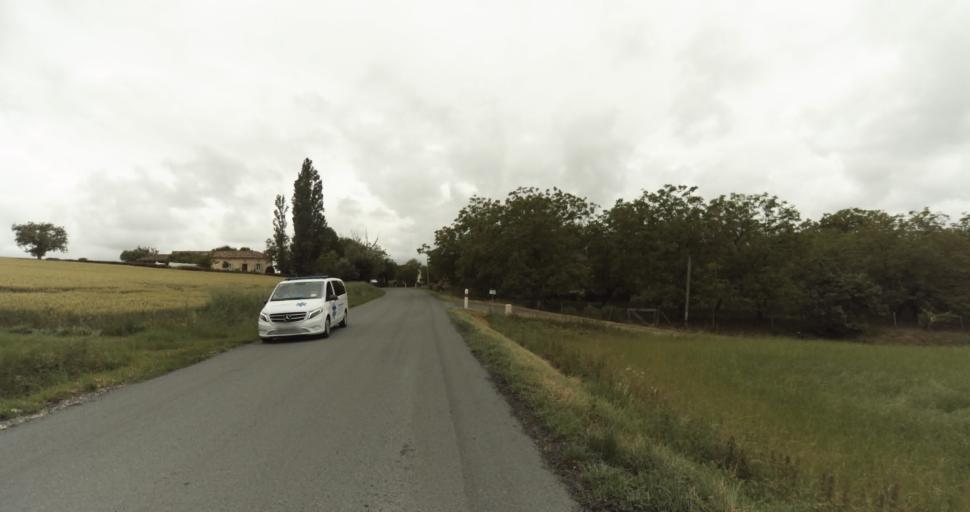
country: FR
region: Aquitaine
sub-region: Departement de la Dordogne
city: Beaumont-du-Perigord
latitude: 44.7057
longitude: 0.8322
